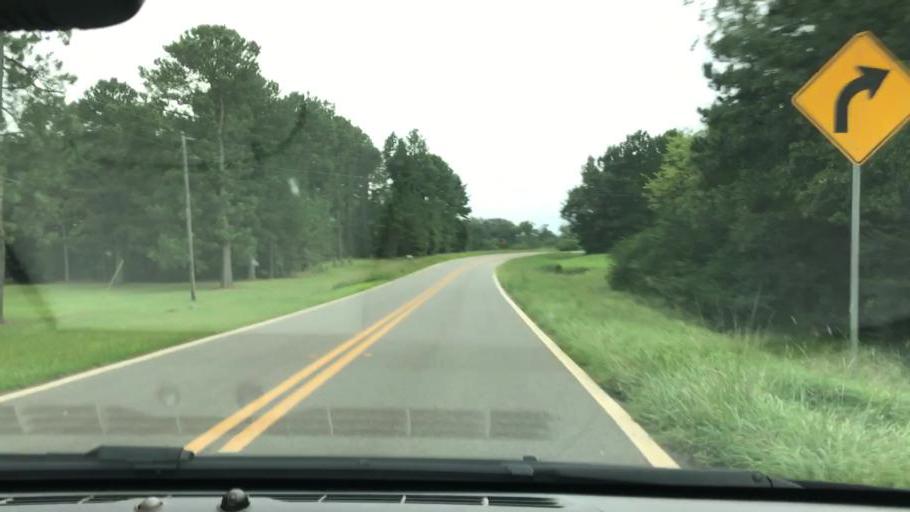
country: US
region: Georgia
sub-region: Early County
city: Blakely
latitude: 31.4450
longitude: -84.9133
